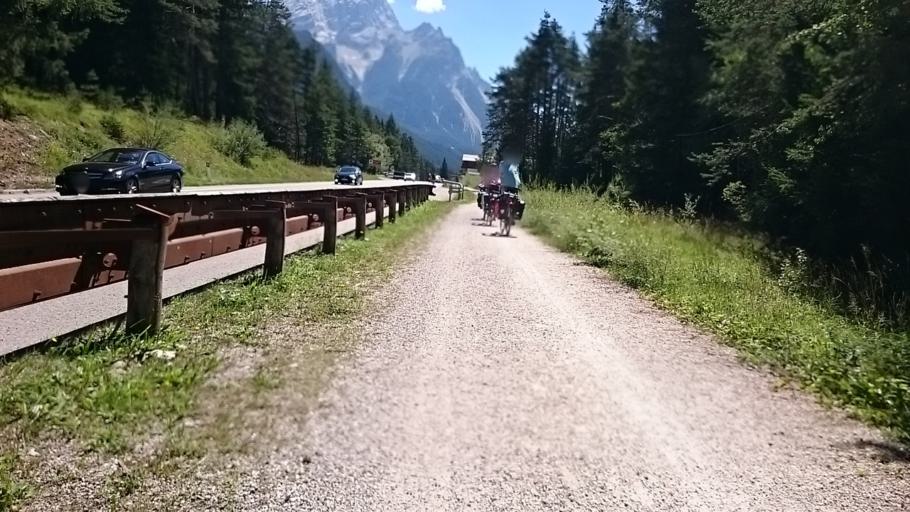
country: IT
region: Veneto
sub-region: Provincia di Belluno
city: San Vito
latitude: 46.4925
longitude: 12.1808
